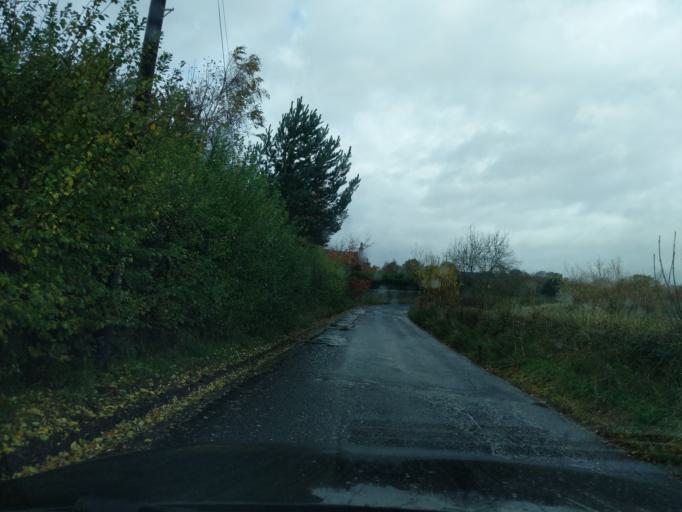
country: GB
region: Scotland
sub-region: Edinburgh
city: Ratho
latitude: 55.9174
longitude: -3.3509
